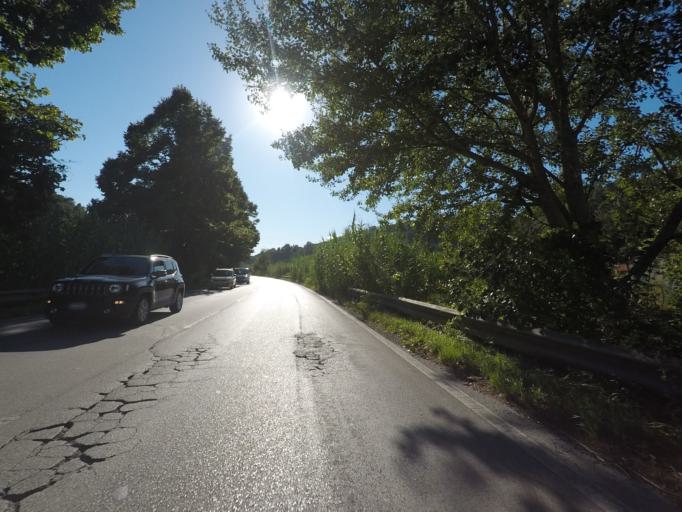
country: IT
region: Tuscany
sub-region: Provincia di Lucca
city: Piano di Mommio
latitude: 43.9372
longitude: 10.2902
